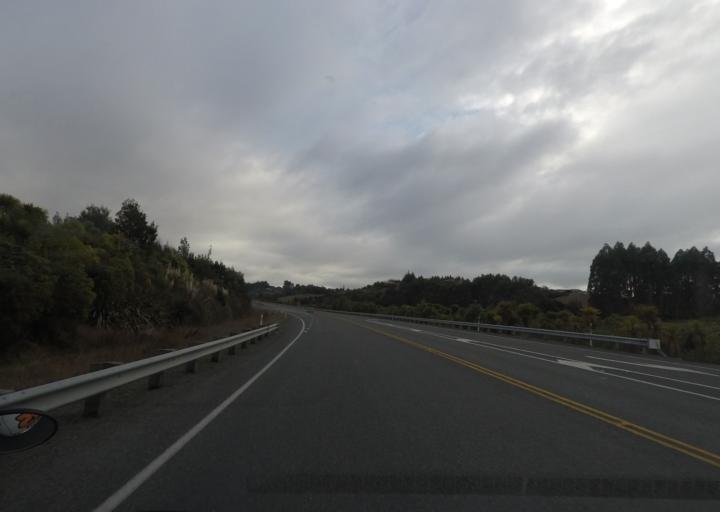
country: NZ
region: Tasman
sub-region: Tasman District
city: Mapua
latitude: -41.2525
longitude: 173.0704
